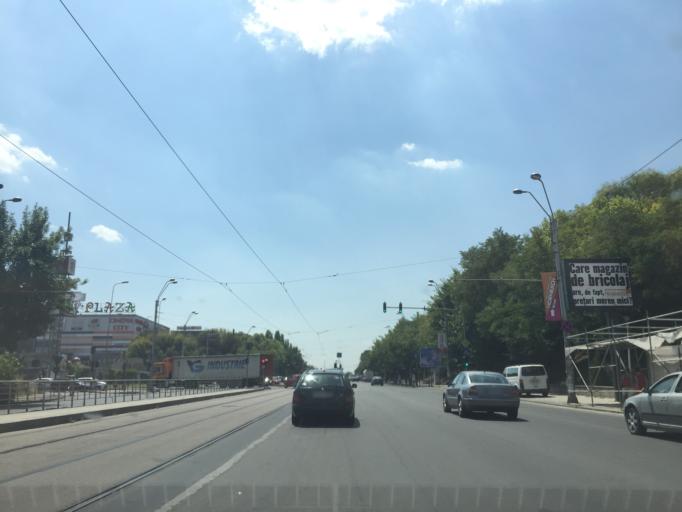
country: RO
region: Bucuresti
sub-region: Municipiul Bucuresti
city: Bucharest
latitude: 44.3988
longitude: 26.1208
